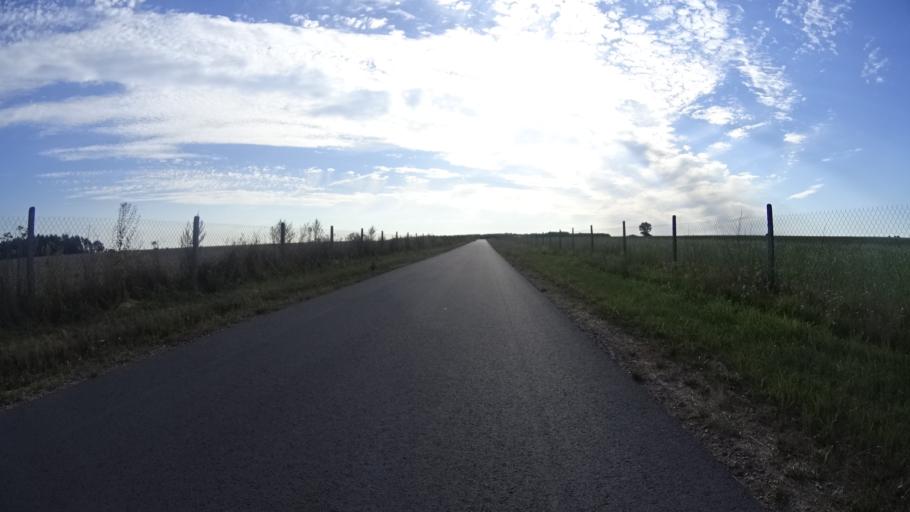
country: PL
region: Masovian Voivodeship
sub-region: Powiat bialobrzeski
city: Wysmierzyce
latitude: 51.6784
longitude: 20.8265
